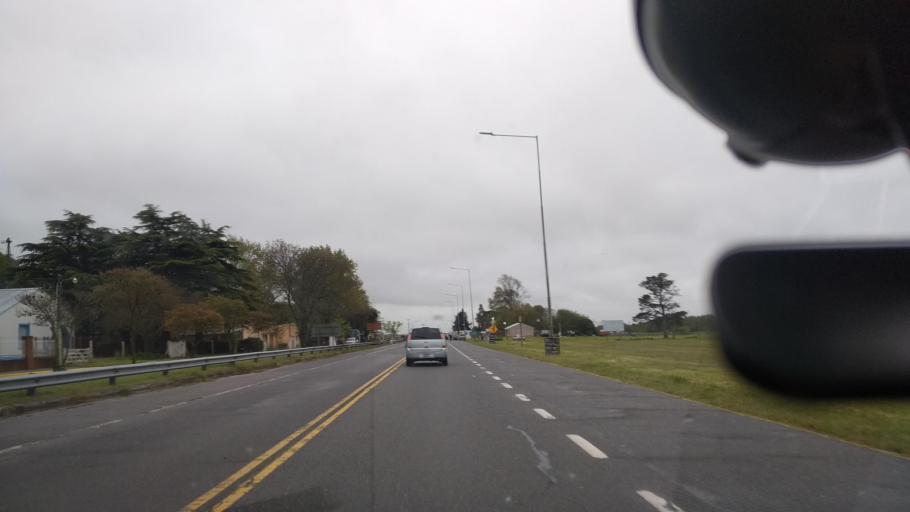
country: AR
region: Buenos Aires
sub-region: Partido de Castelli
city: Castelli
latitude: -35.9760
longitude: -57.4496
